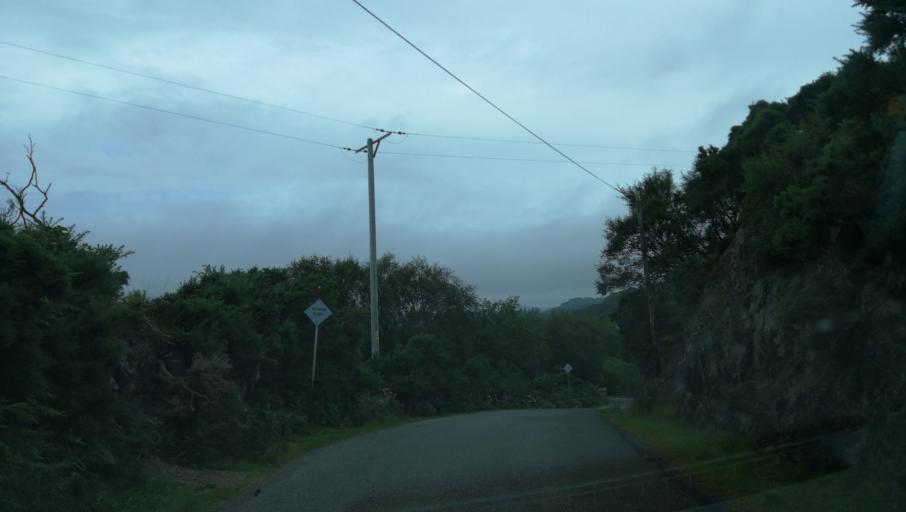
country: GB
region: Scotland
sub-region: Highland
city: Ullapool
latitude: 58.1361
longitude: -5.2621
